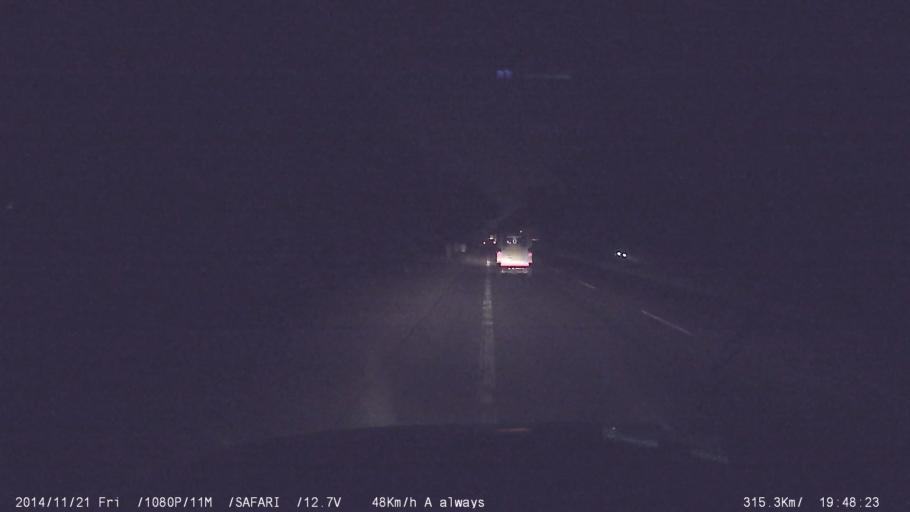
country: IN
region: Tamil Nadu
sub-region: Kancheepuram
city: Singapperumalkovil
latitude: 12.7812
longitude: 80.0124
